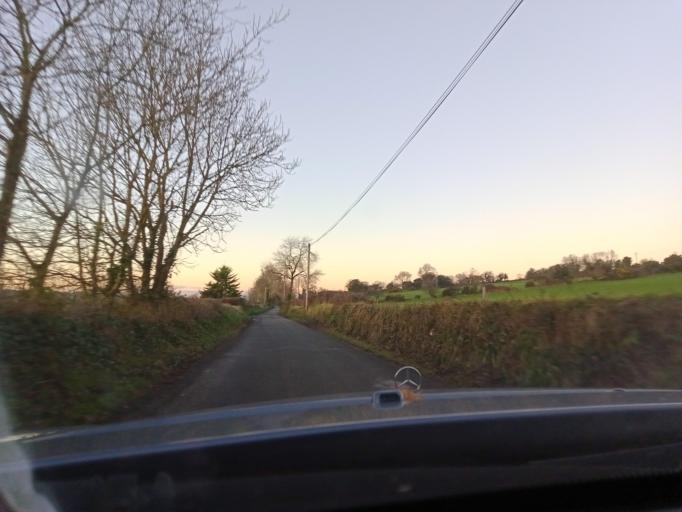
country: IE
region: Leinster
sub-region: Kilkenny
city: Thomastown
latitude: 52.4512
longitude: -7.1028
